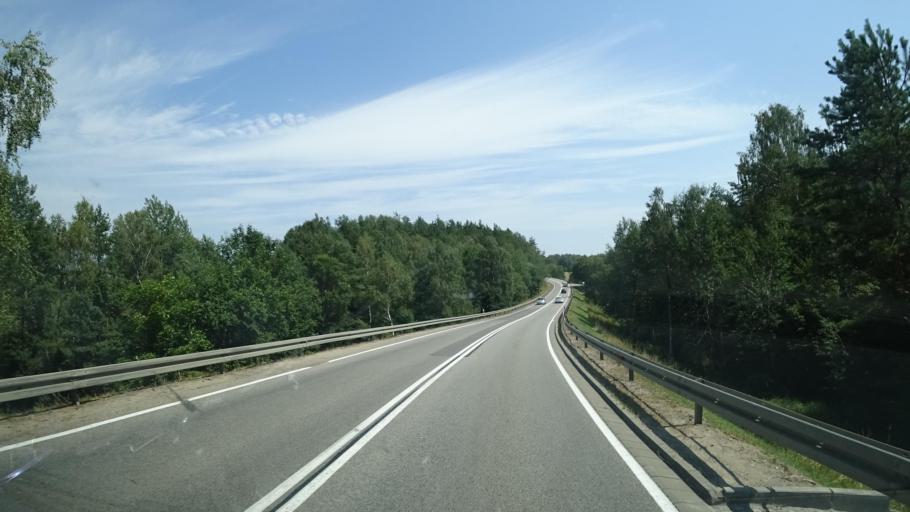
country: PL
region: Pomeranian Voivodeship
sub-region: Powiat koscierski
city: Grabowo Koscierskie
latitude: 54.2229
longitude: 18.1439
